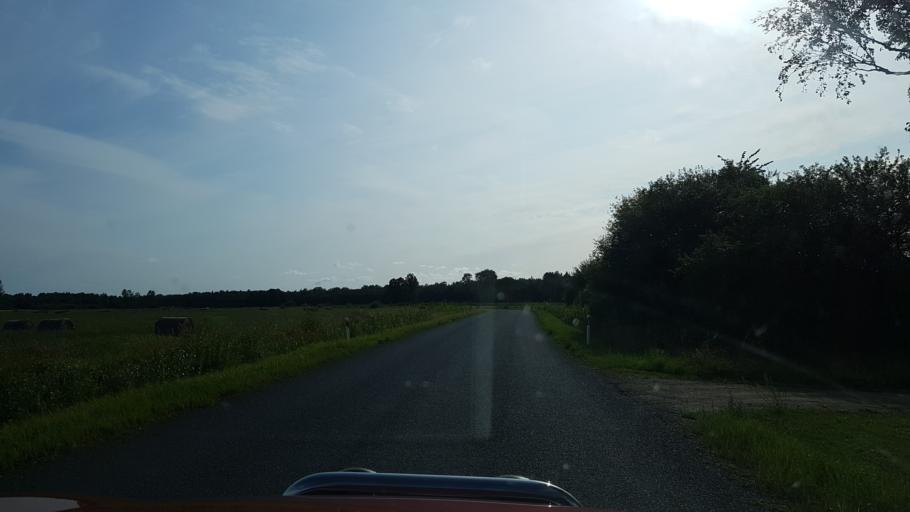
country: EE
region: Laeaene
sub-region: Lihula vald
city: Lihula
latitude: 58.3806
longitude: 24.0032
